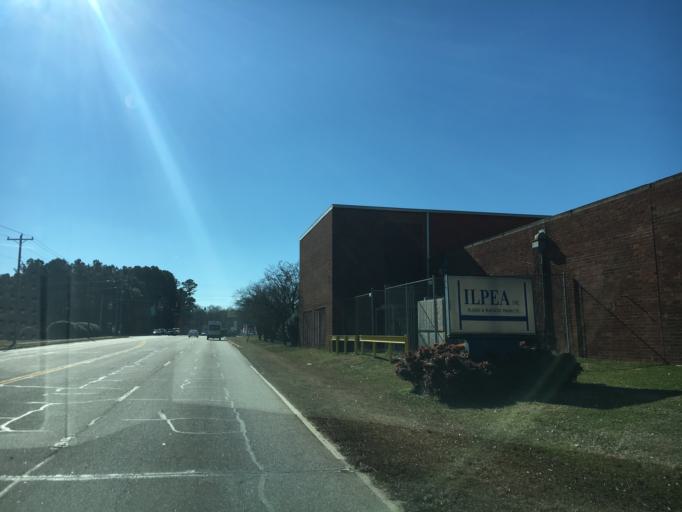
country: US
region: South Carolina
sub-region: Anderson County
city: Anderson
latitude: 34.4865
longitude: -82.6347
